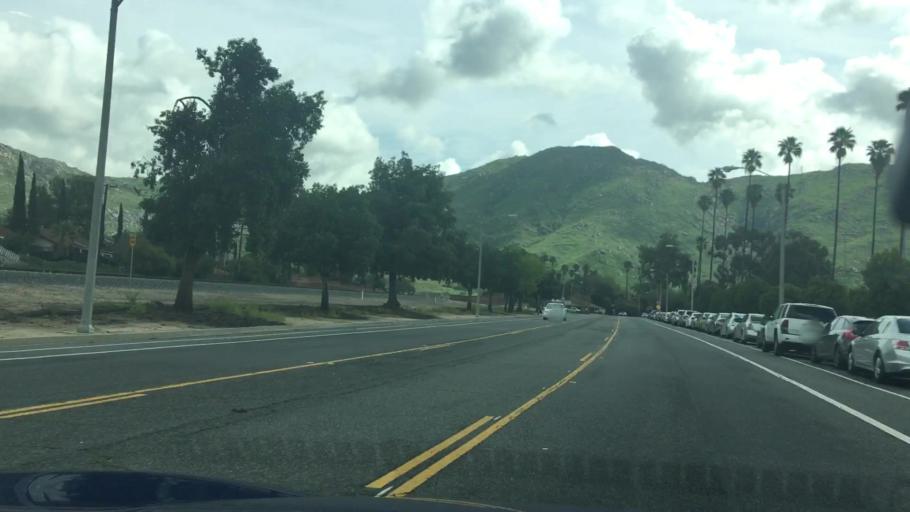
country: US
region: California
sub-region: Riverside County
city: Highgrove
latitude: 33.9797
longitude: -117.3203
